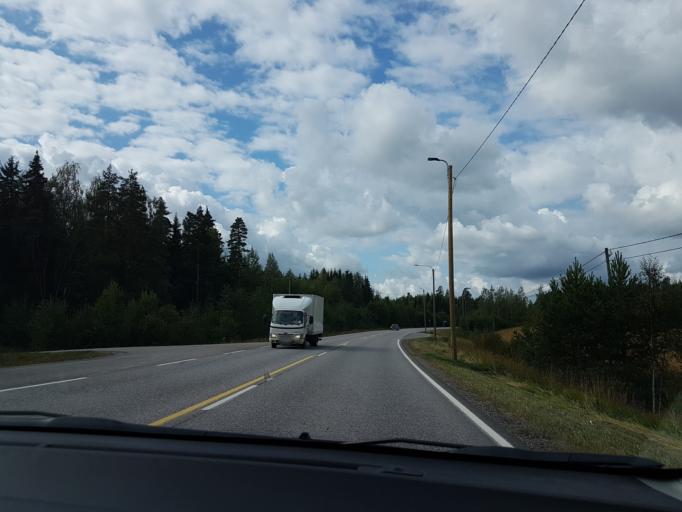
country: FI
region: Uusimaa
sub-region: Helsinki
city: Pornainen
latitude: 60.4797
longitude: 25.3372
